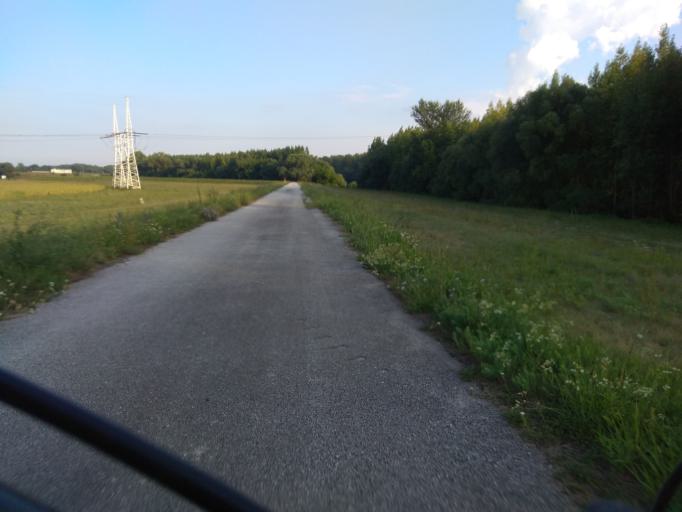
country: SK
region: Trnavsky
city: Gabcikovo
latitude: 47.8017
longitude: 17.6490
